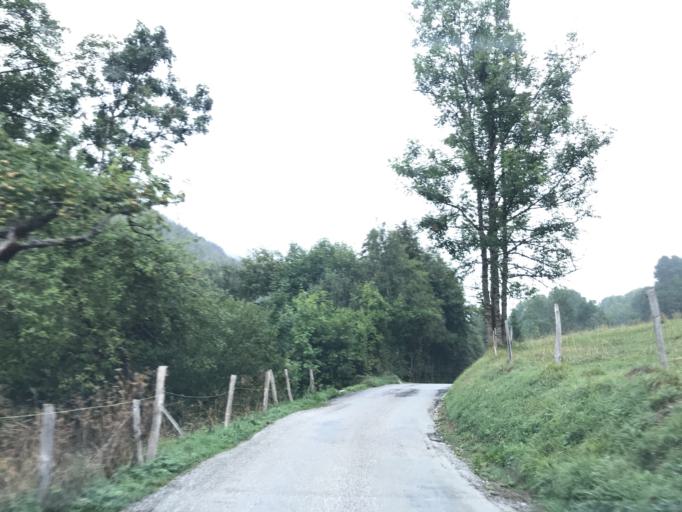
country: FR
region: Rhone-Alpes
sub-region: Departement de la Haute-Savoie
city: Talloires
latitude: 45.8144
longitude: 6.2612
